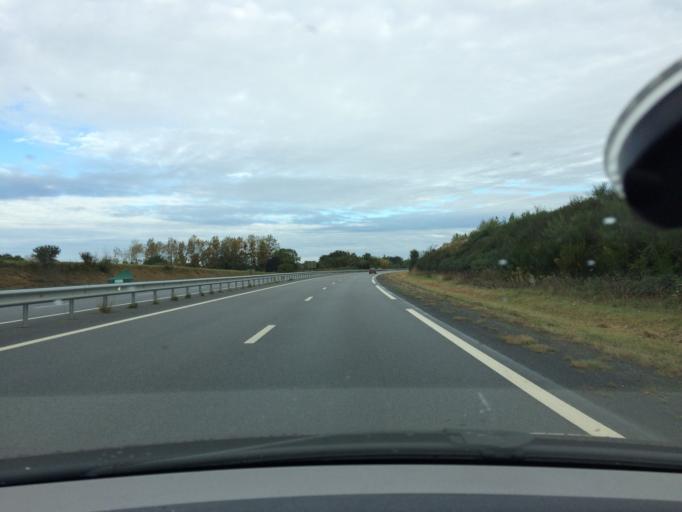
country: FR
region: Brittany
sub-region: Departement d'Ille-et-Vilaine
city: Corps-Nuds
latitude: 47.9793
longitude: -1.5624
